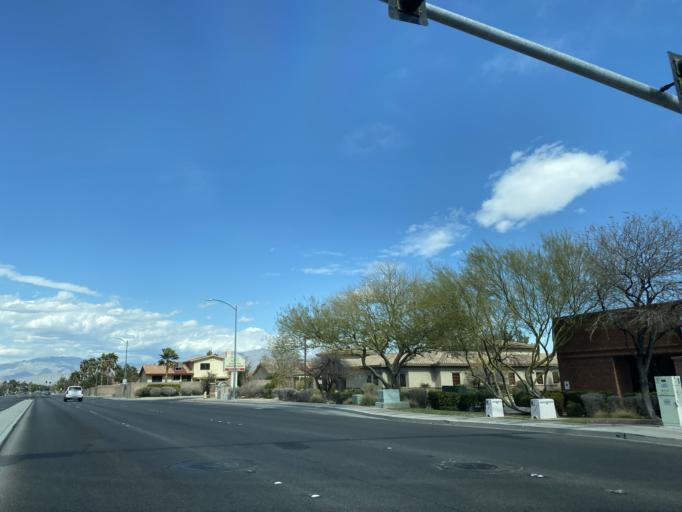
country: US
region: Nevada
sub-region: Clark County
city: Spring Valley
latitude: 36.2257
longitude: -115.2606
